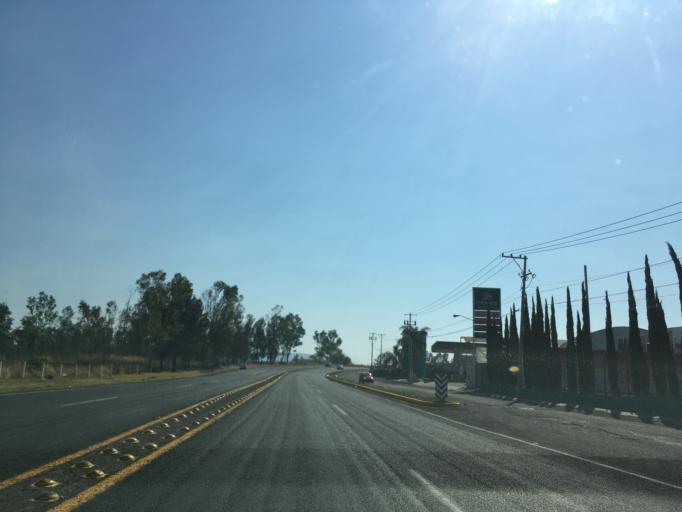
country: MX
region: Michoacan
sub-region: Morelia
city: La Aldea
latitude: 19.7336
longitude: -101.1310
